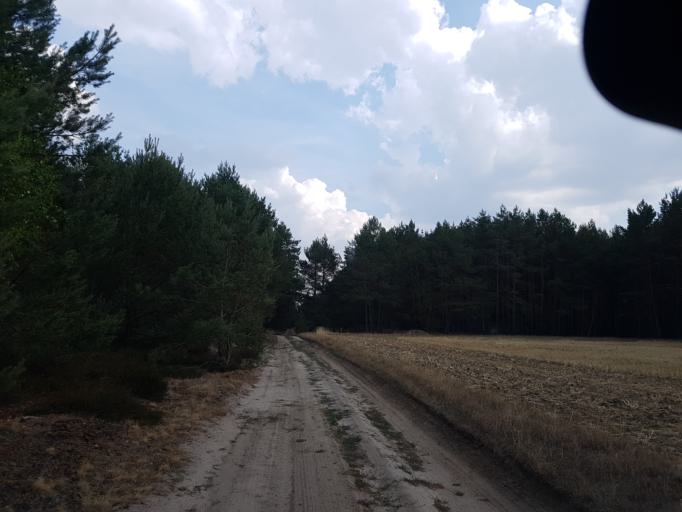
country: DE
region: Brandenburg
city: Treuenbrietzen
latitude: 52.0343
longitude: 12.8762
